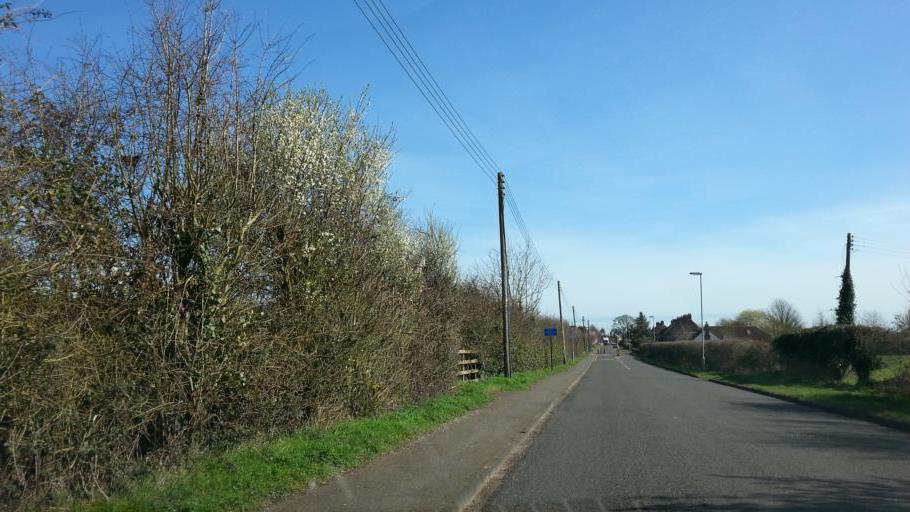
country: GB
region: England
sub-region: Cambridgeshire
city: Swavesey
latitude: 52.3128
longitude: 0.0085
